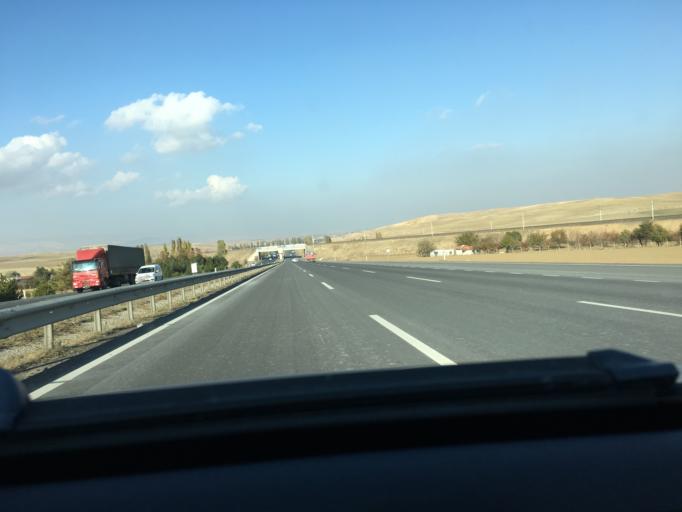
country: TR
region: Ankara
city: Polatli
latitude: 39.6203
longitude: 32.1898
